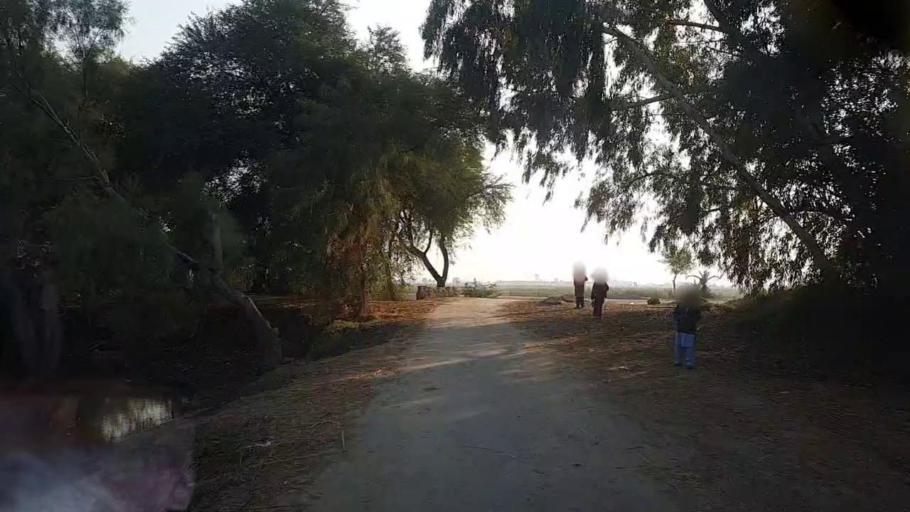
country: PK
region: Sindh
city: Jacobabad
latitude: 28.2311
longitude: 68.4866
